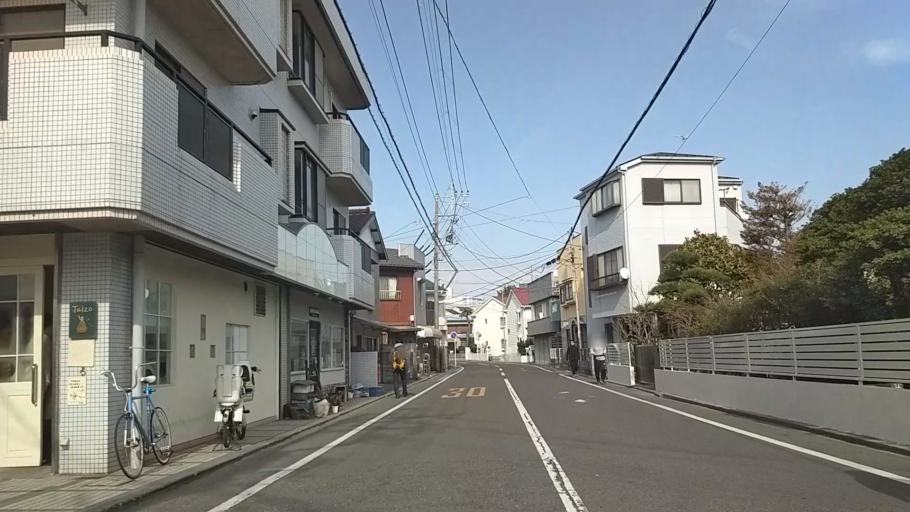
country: JP
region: Kanagawa
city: Chigasaki
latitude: 35.3249
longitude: 139.4020
